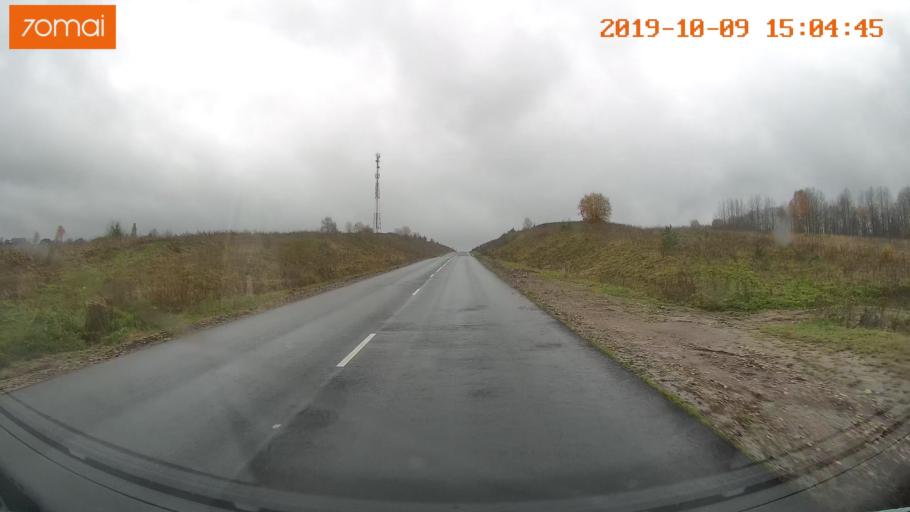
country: RU
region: Kostroma
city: Chistyye Bory
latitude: 58.2547
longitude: 41.6640
